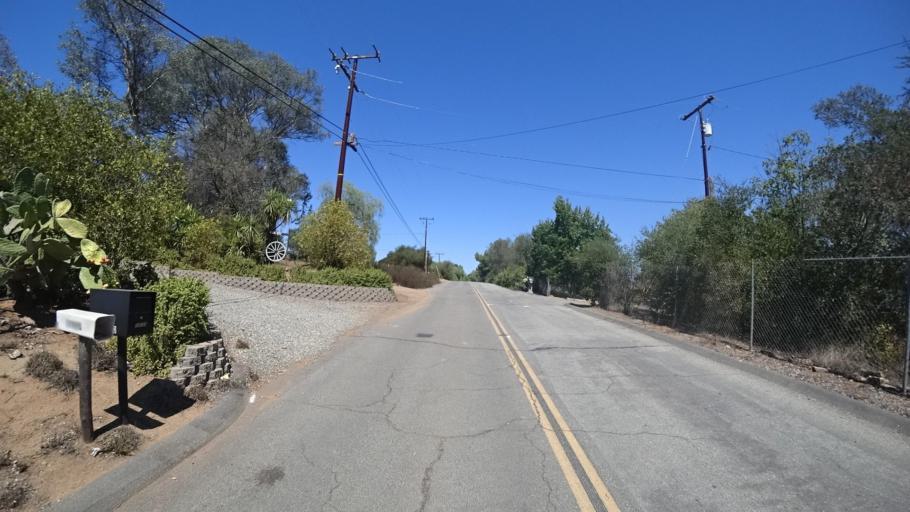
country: US
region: California
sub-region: San Diego County
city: Valley Center
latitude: 33.2754
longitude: -117.0416
